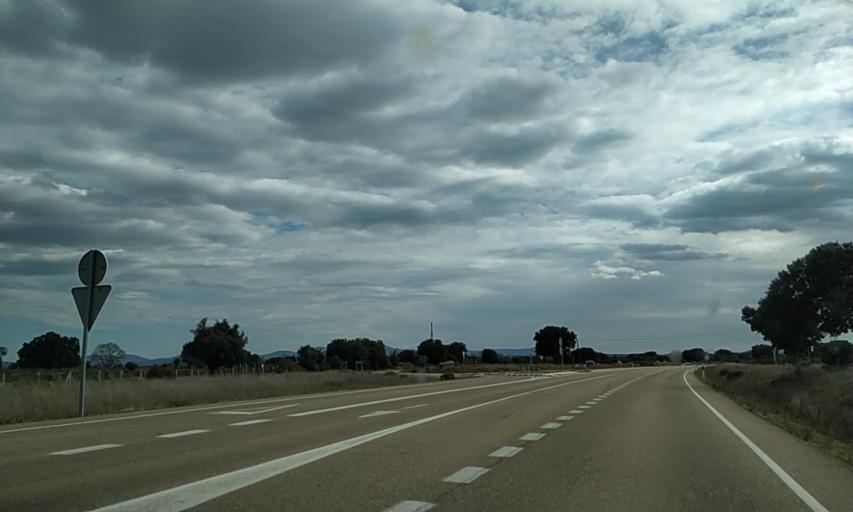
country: ES
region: Castille and Leon
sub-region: Provincia de Salamanca
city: Robleda
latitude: 40.4525
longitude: -6.5914
